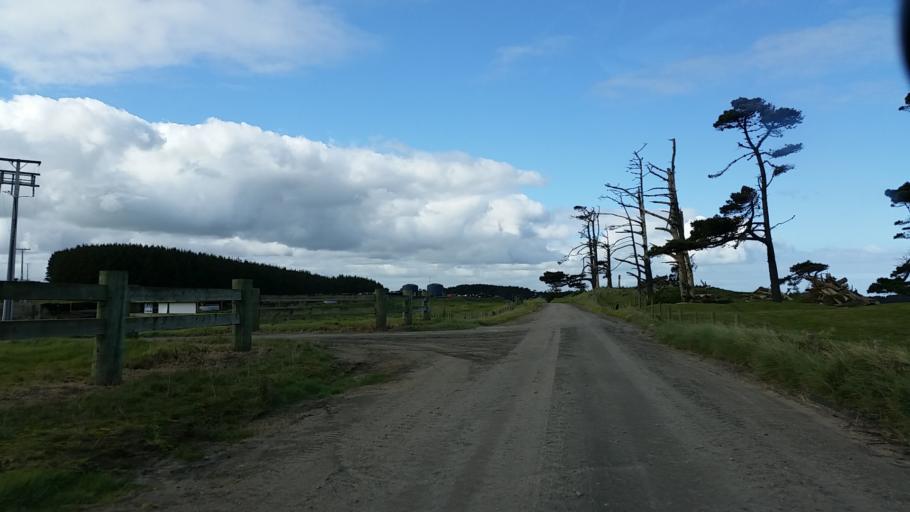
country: NZ
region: Taranaki
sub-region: South Taranaki District
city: Patea
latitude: -39.7997
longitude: 174.5971
